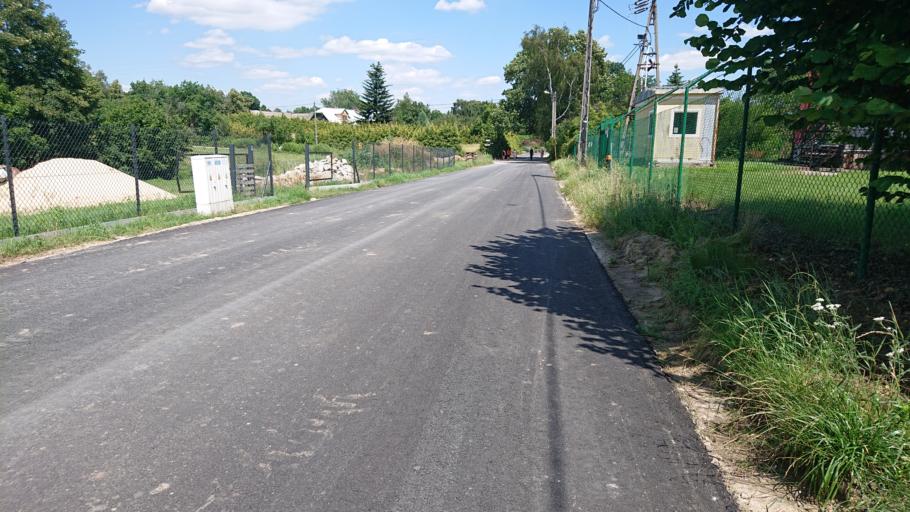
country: PL
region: Lublin Voivodeship
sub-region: Powiat pulawski
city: Kazimierz Dolny
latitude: 51.3255
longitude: 21.9680
